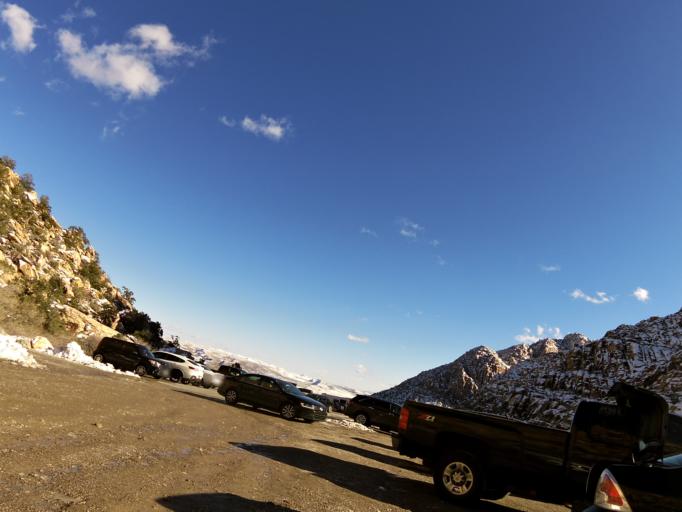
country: US
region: Nevada
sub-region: Clark County
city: Summerlin South
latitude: 36.1612
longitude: -115.4988
